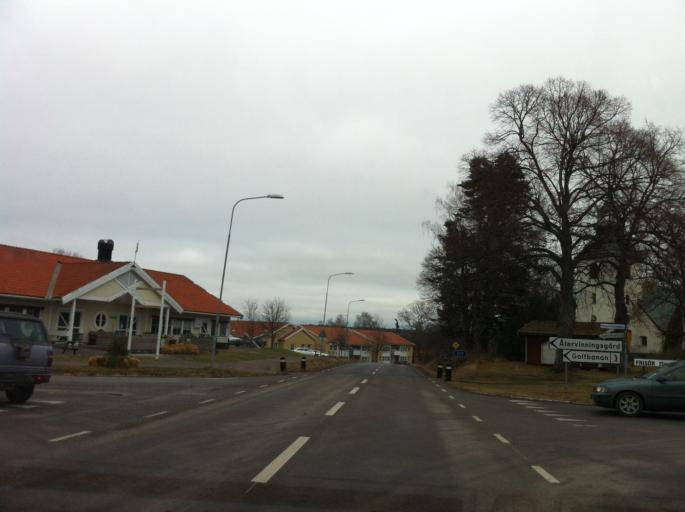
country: SE
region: Kalmar
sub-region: Vasterviks Kommun
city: Overum
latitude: 57.9081
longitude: 16.2494
